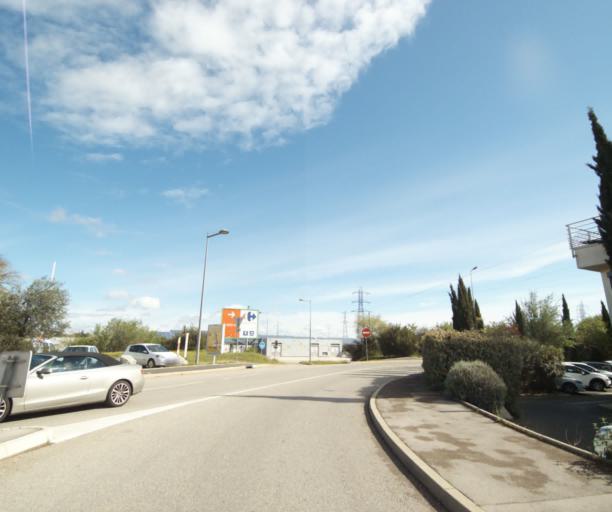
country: FR
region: Languedoc-Roussillon
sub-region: Departement de l'Herault
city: Saint-Jean-de-Vedas
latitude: 43.5703
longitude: 3.8382
